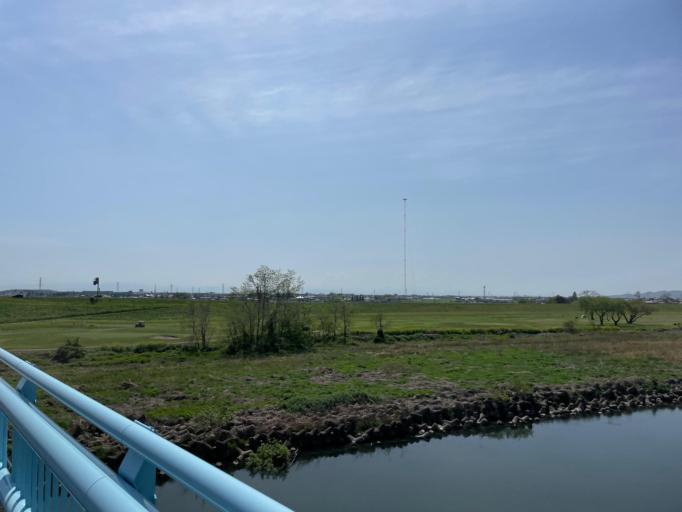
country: JP
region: Tochigi
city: Ashikaga
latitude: 36.3030
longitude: 139.4980
